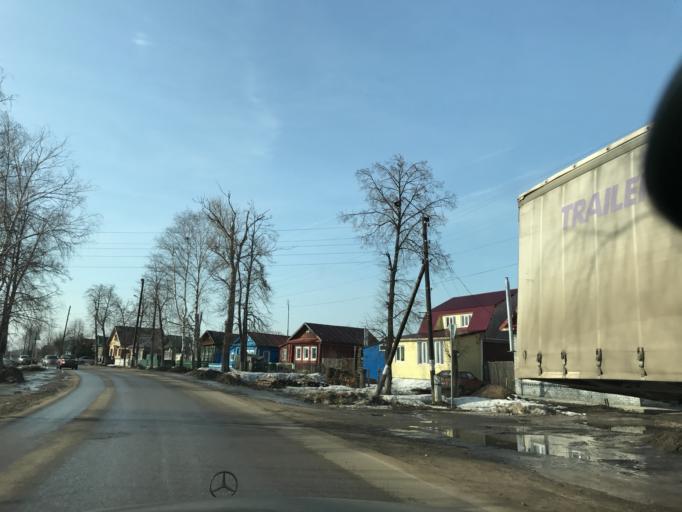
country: RU
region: Nizjnij Novgorod
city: Pavlovo
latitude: 55.9962
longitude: 43.0388
